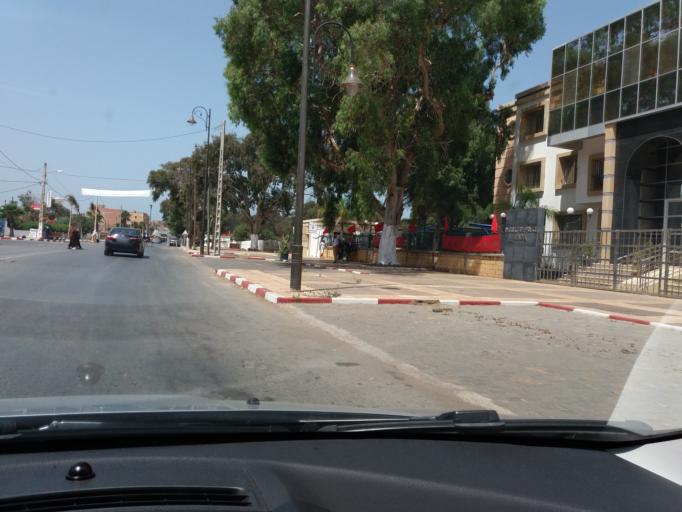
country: MA
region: Gharb-Chrarda-Beni Hssen
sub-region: Kenitra Province
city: Kenitra
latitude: 34.2663
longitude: -6.6460
